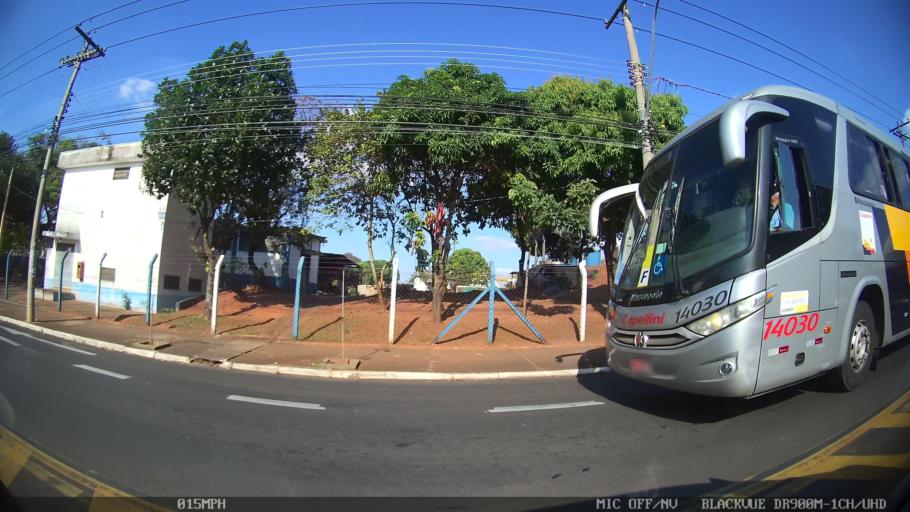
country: BR
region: Sao Paulo
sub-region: Nova Odessa
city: Nova Odessa
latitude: -22.7864
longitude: -47.3016
